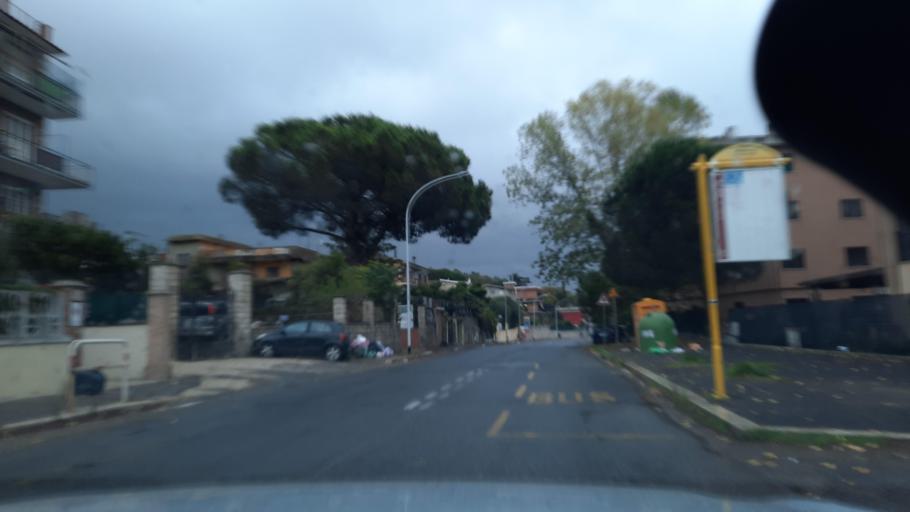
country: IT
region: Latium
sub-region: Citta metropolitana di Roma Capitale
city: Ponte Galeria-La Pisana
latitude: 41.8197
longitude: 12.3531
